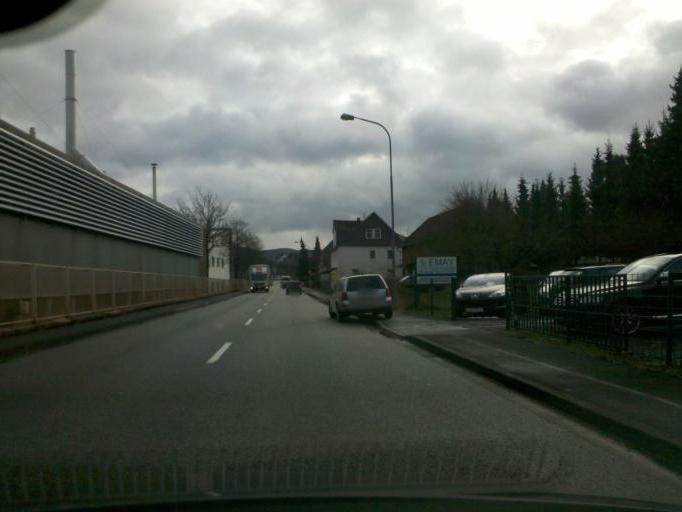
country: DE
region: Hesse
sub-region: Regierungsbezirk Giessen
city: Biedenkopf
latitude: 50.8672
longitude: 8.5498
